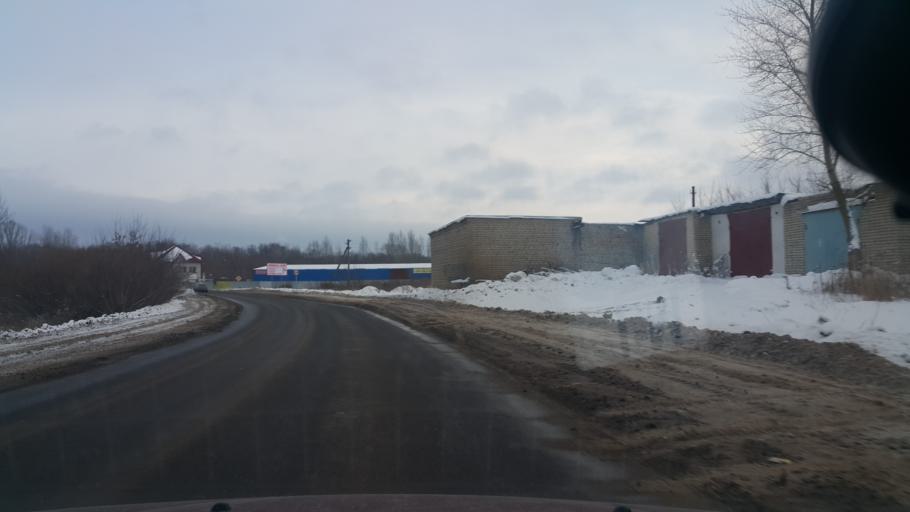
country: RU
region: Tambov
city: Bokino
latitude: 52.6588
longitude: 41.4378
